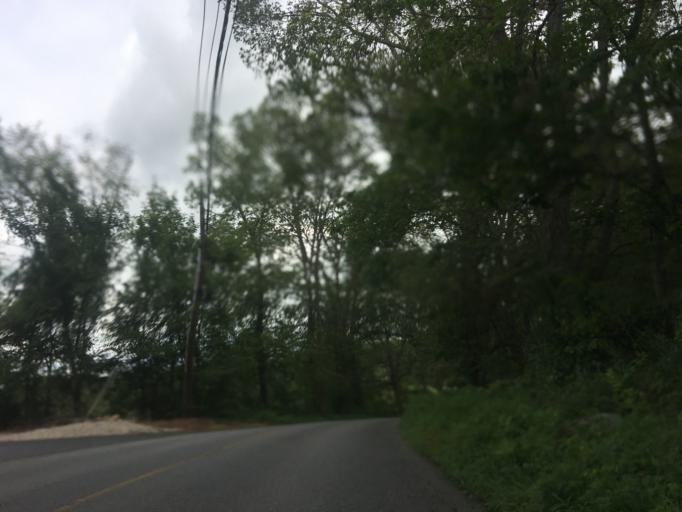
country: US
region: Connecticut
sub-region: Windham County
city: East Brooklyn
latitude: 41.7941
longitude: -71.9310
